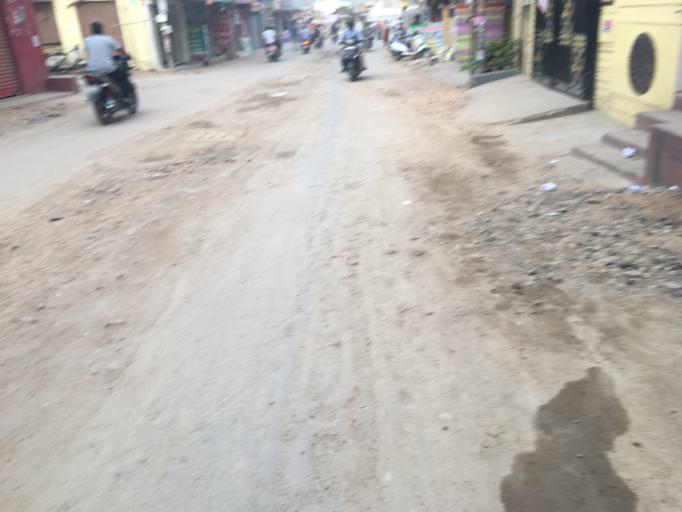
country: IN
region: Telangana
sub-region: Rangareddi
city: Gaddi Annaram
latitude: 17.3707
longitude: 78.5269
